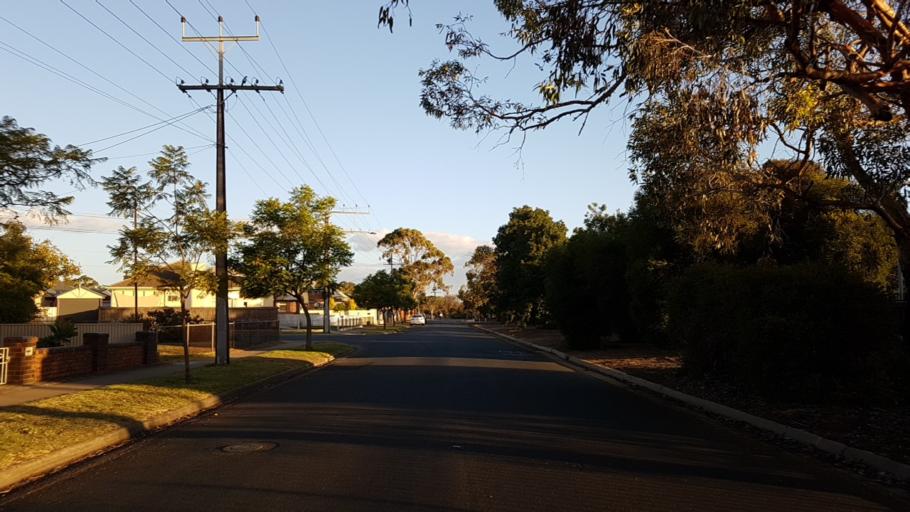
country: AU
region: South Australia
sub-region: Port Adelaide Enfield
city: Alberton
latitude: -34.8648
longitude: 138.5241
